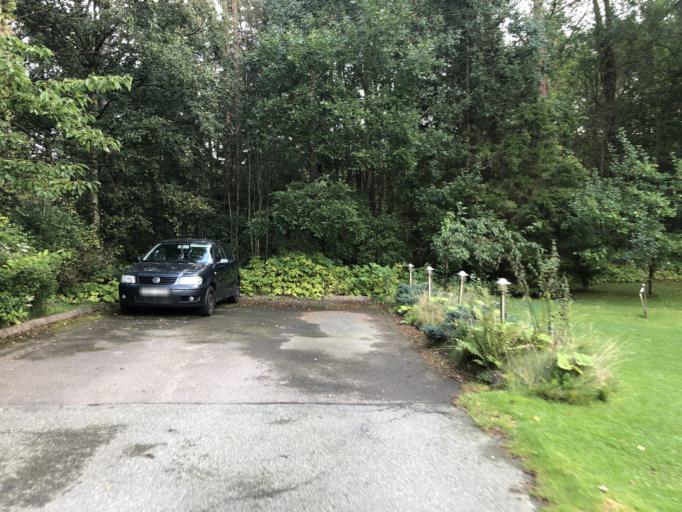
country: SE
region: Vaestra Goetaland
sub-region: Goteborg
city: Majorna
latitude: 57.7411
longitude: 11.8938
